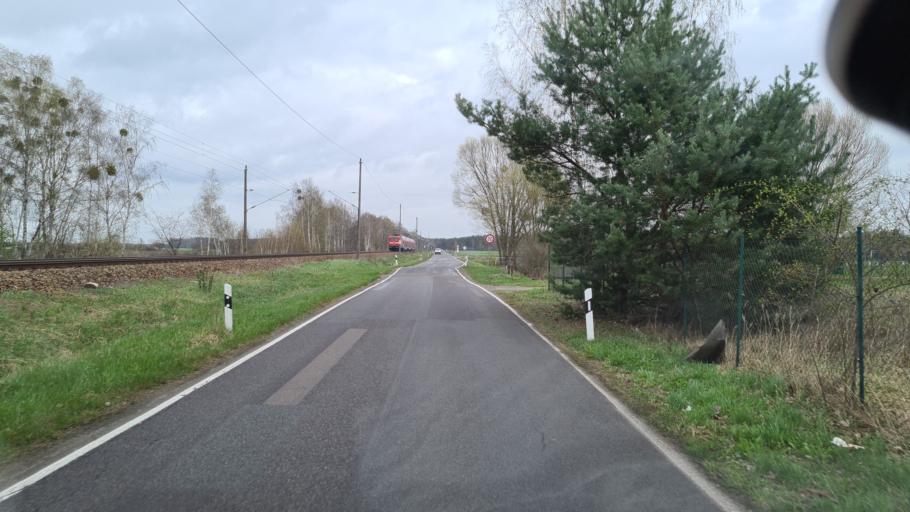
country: DE
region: Brandenburg
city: Ruhland
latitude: 51.4582
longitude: 13.8876
